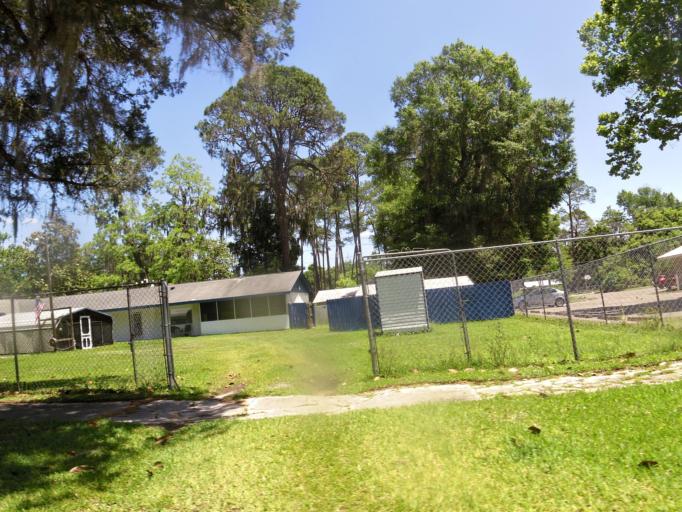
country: US
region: Florida
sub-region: Bradford County
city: Starke
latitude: 29.9467
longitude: -82.1068
